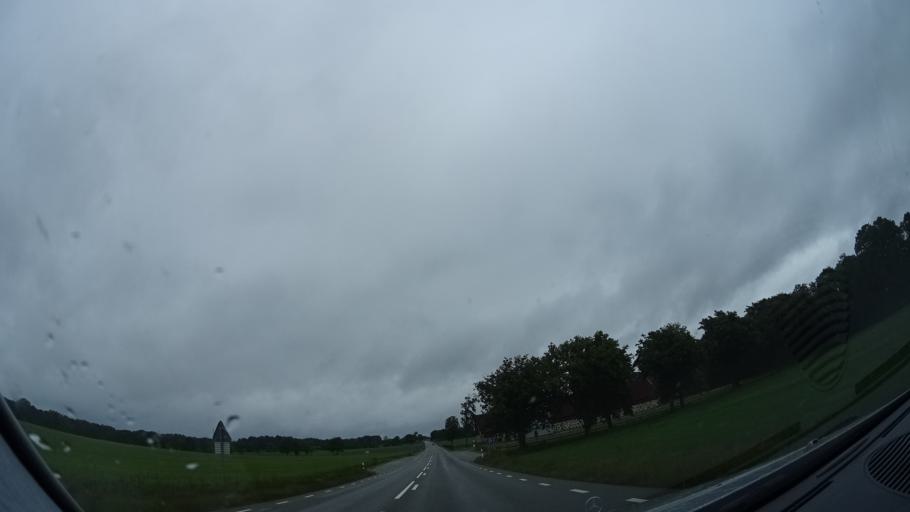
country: SE
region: Skane
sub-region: Hoors Kommun
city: Loberod
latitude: 55.8532
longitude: 13.4992
